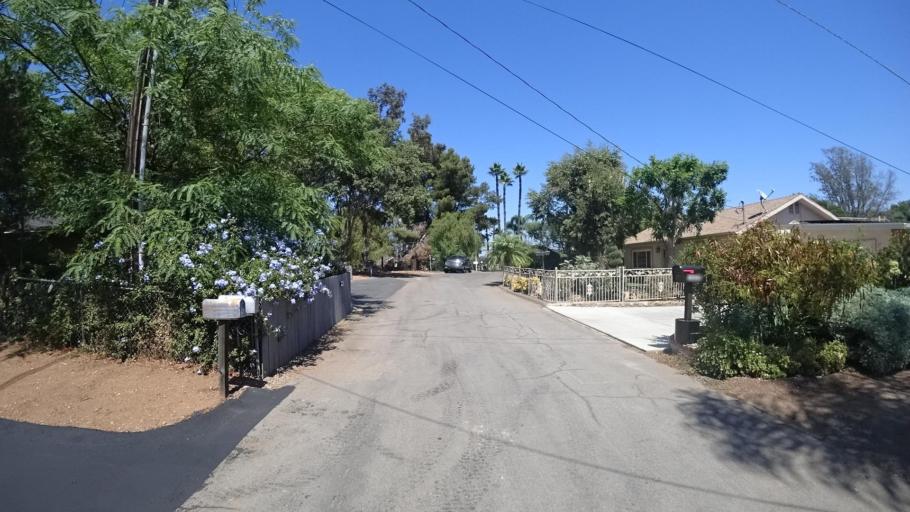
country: US
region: California
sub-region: San Diego County
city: Fallbrook
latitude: 33.3909
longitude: -117.2492
